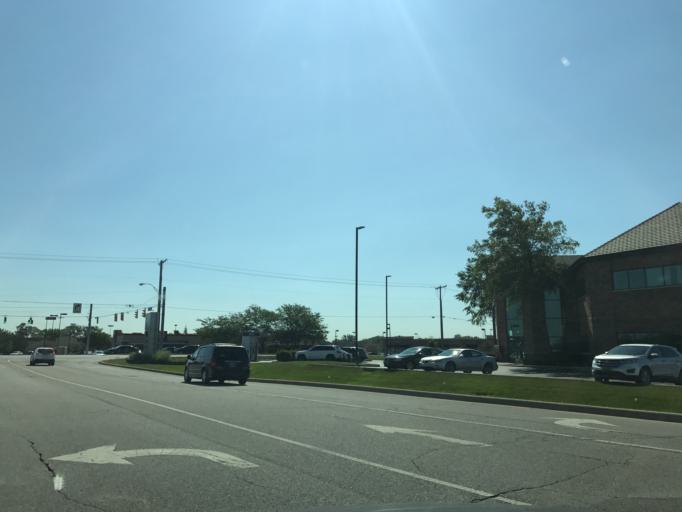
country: US
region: Indiana
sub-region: Lake County
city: Highland
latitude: 41.5267
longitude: -87.4724
